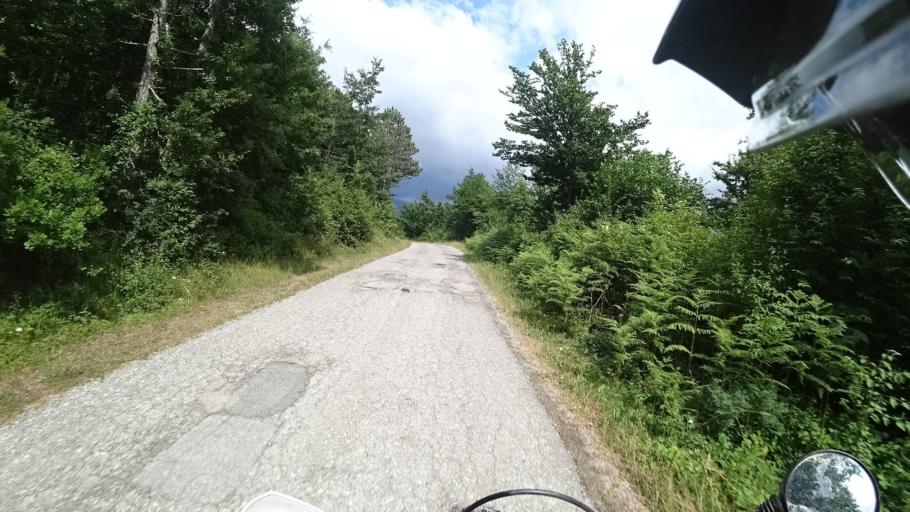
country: HR
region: Zadarska
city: Gracac
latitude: 44.5241
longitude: 15.7876
